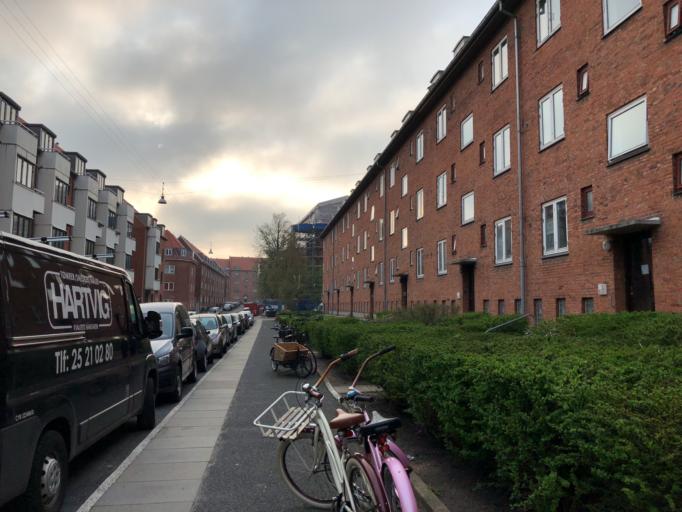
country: DK
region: Capital Region
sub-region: Kobenhavn
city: Vanlose
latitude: 55.7045
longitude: 12.4931
